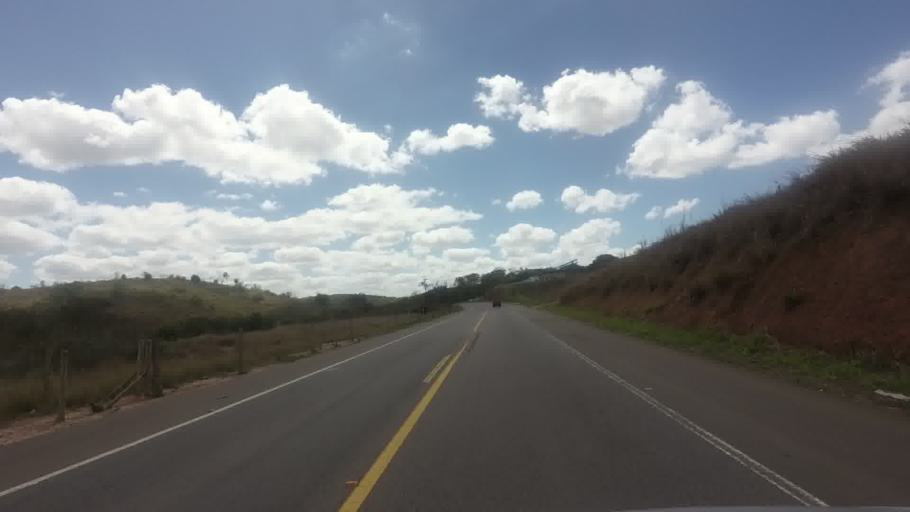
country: BR
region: Minas Gerais
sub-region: Recreio
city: Recreio
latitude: -21.6639
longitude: -42.3800
